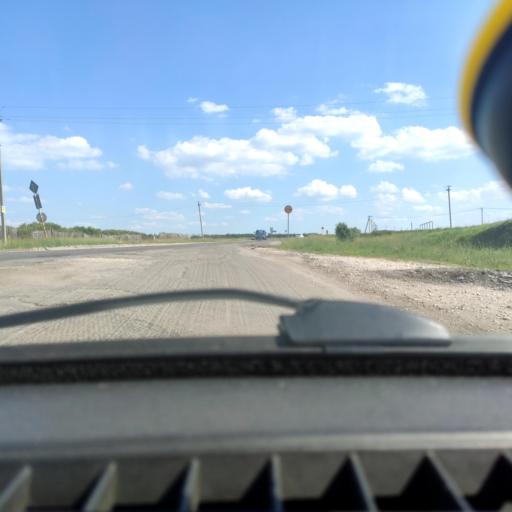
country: RU
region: Samara
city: Povolzhskiy
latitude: 53.7511
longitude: 49.7419
